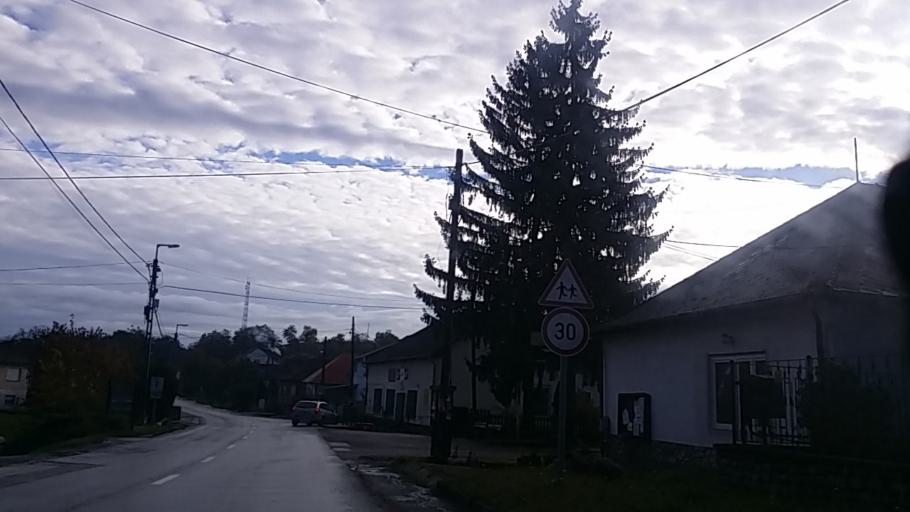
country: HU
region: Heves
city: Szilvasvarad
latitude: 48.1398
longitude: 20.4238
